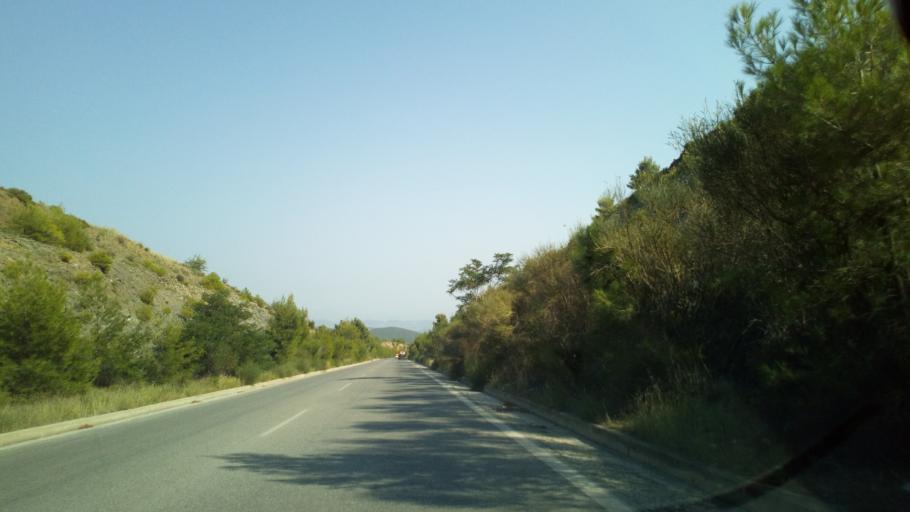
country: GR
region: Central Macedonia
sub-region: Nomos Chalkidikis
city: Polygyros
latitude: 40.3540
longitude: 23.4436
